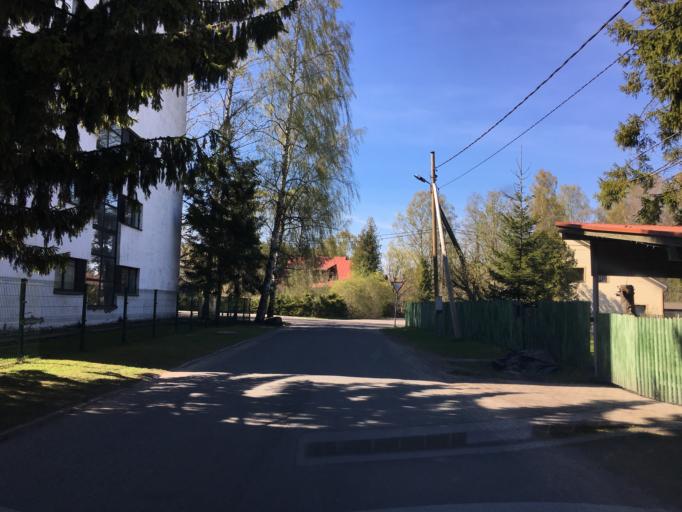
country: EE
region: Harju
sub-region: Saue vald
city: Laagri
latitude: 59.3909
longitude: 24.6545
